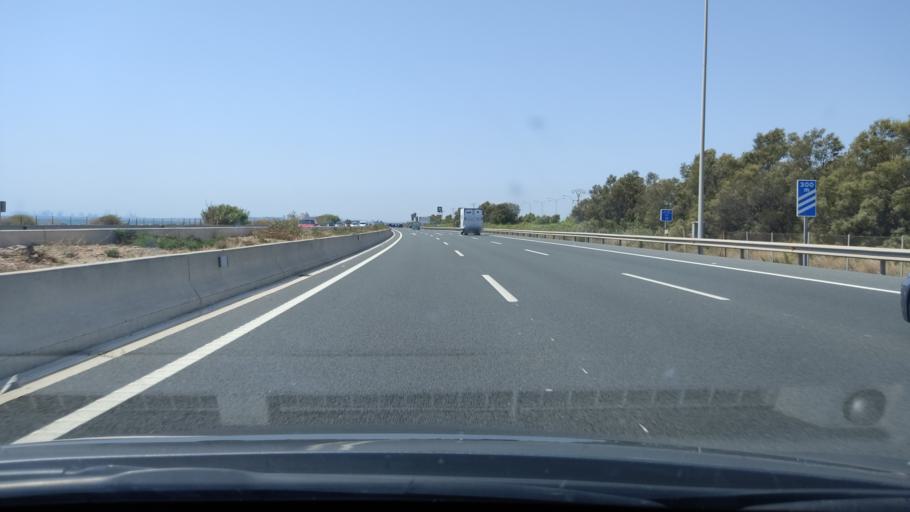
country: ES
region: Valencia
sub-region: Provincia de Valencia
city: Albuixech
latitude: 39.5360
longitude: -0.3084
